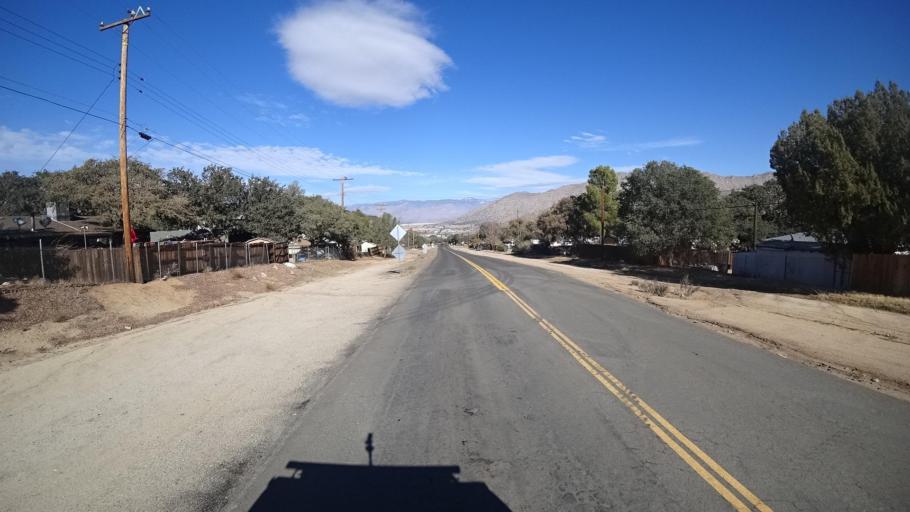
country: US
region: California
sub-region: Kern County
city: Bodfish
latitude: 35.5866
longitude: -118.4975
